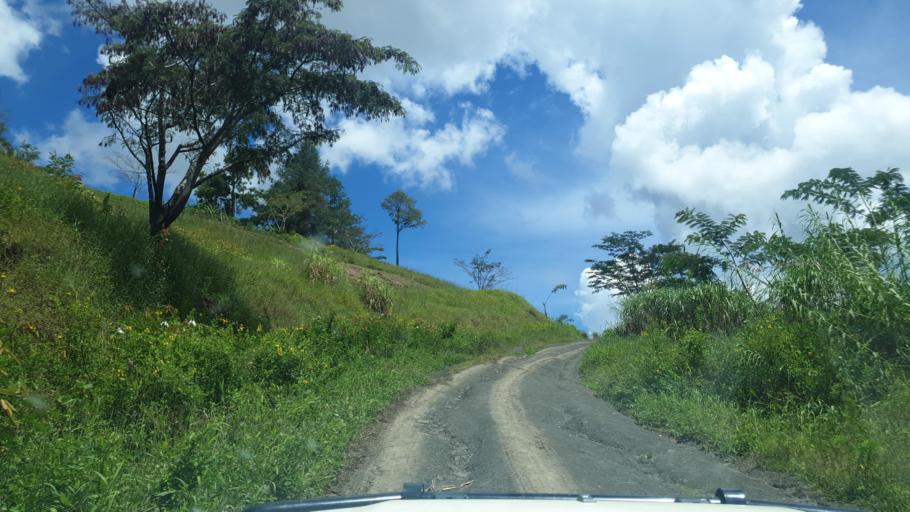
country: PG
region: Chimbu
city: Kundiawa
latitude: -6.2553
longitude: 145.1391
